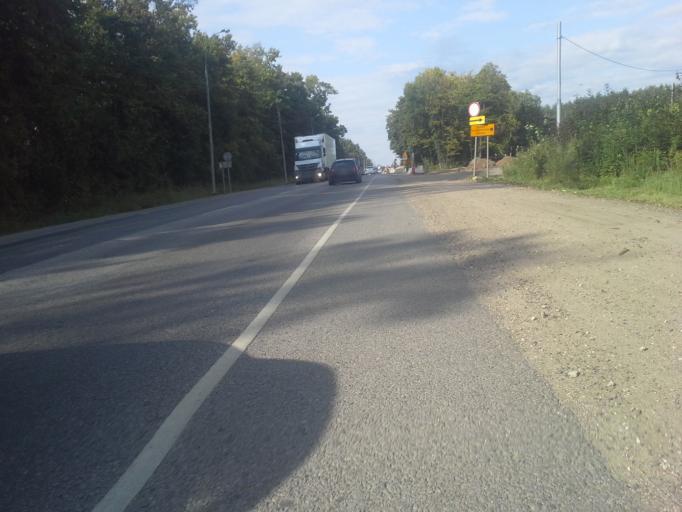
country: RU
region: Moskovskaya
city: Selyatino
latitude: 55.5533
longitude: 36.9871
